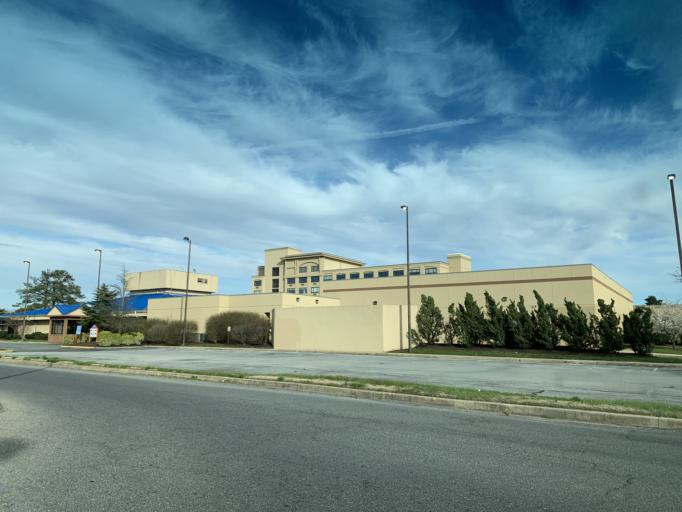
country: US
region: Delaware
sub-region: Kent County
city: Cheswold
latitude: 39.1949
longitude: -75.5514
